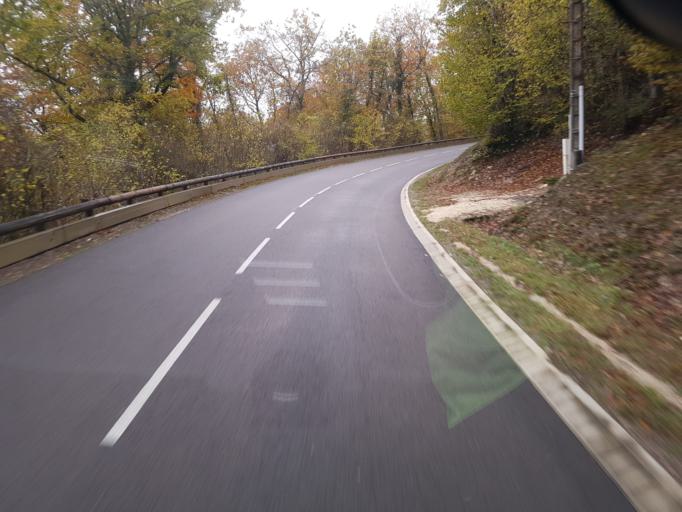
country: FR
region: Bourgogne
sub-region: Departement de la Cote-d'Or
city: Messigny-et-Vantoux
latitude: 47.5485
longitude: 4.9189
